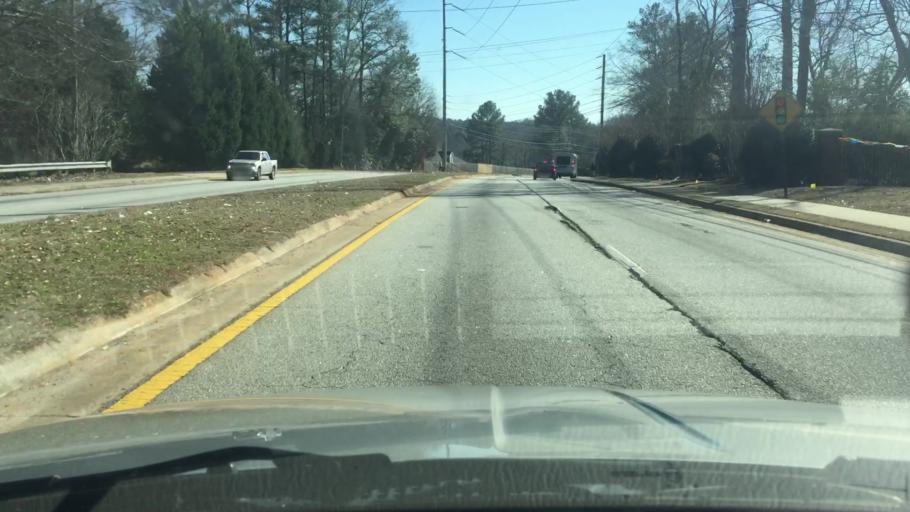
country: US
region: Georgia
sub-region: DeKalb County
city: Redan
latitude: 33.7399
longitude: -84.1951
